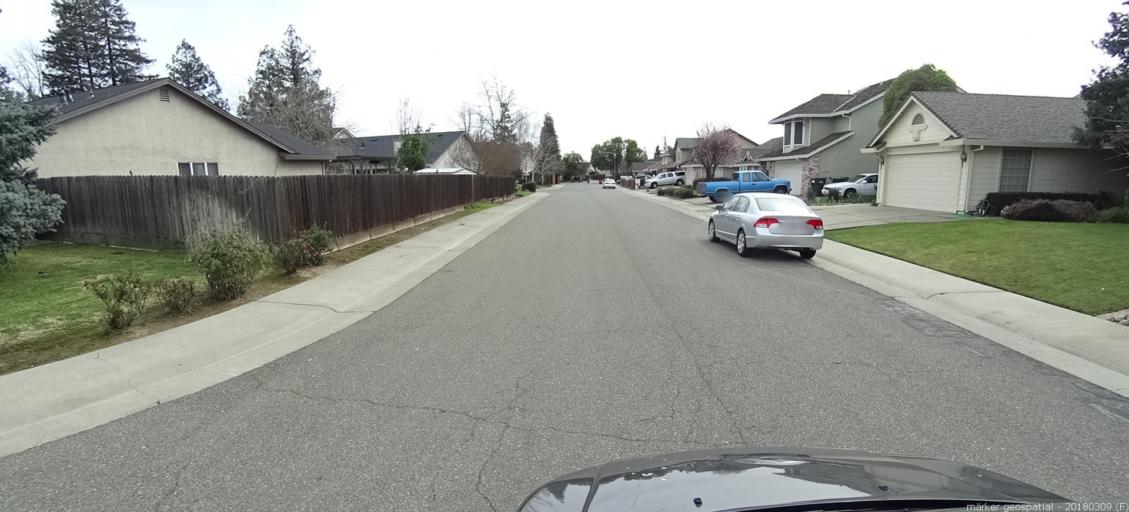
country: US
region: California
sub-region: Sacramento County
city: Vineyard
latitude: 38.4660
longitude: -121.3848
